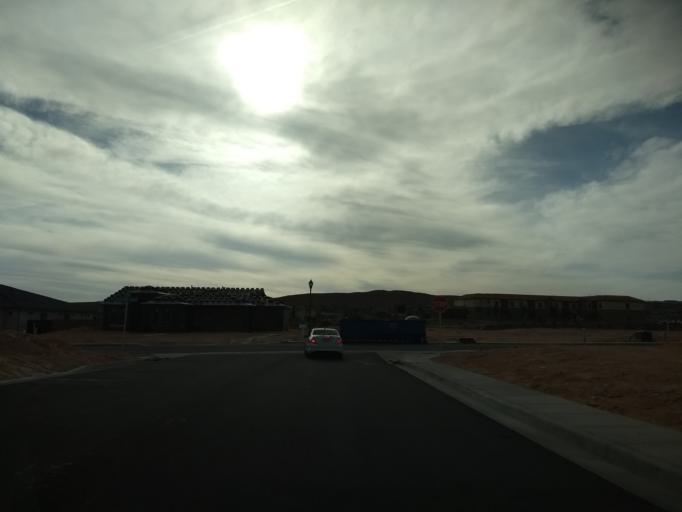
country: US
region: Utah
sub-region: Washington County
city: Washington
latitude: 37.1460
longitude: -113.5176
